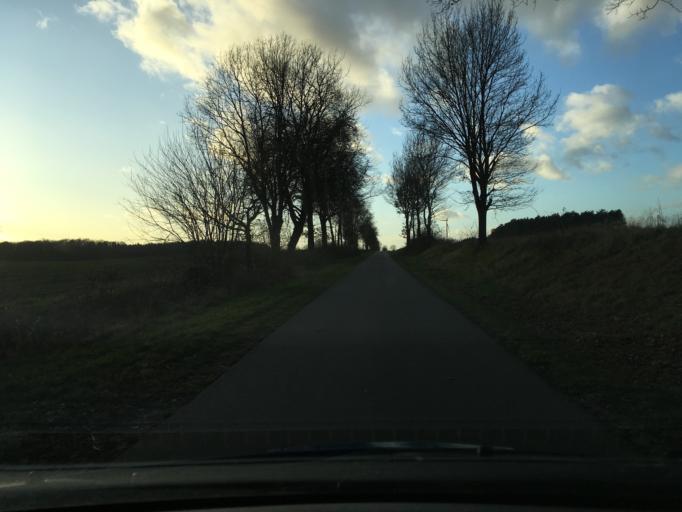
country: DE
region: Lower Saxony
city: Rehlingen
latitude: 53.1036
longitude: 10.2058
